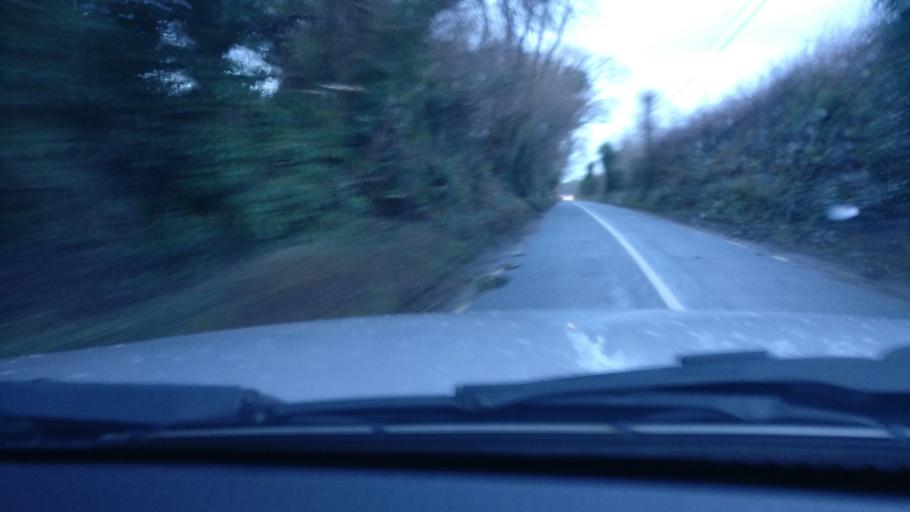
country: IE
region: Connaught
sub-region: County Galway
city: Ballinasloe
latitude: 53.2694
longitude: -8.2487
